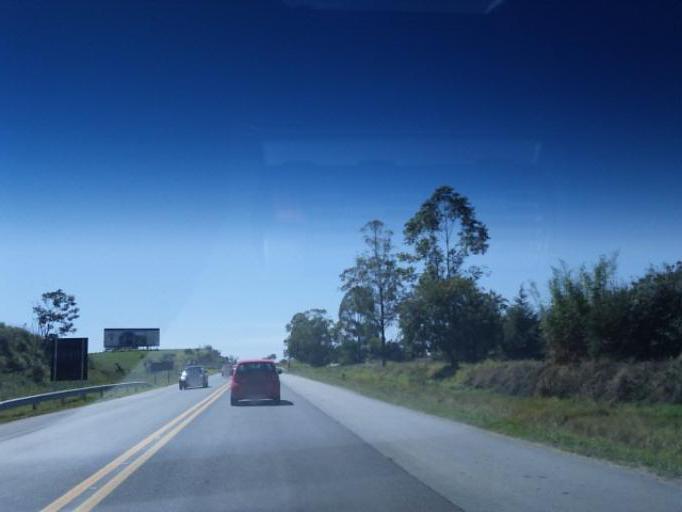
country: BR
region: Sao Paulo
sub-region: Tremembe
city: Tremembe
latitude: -22.9609
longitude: -45.6330
